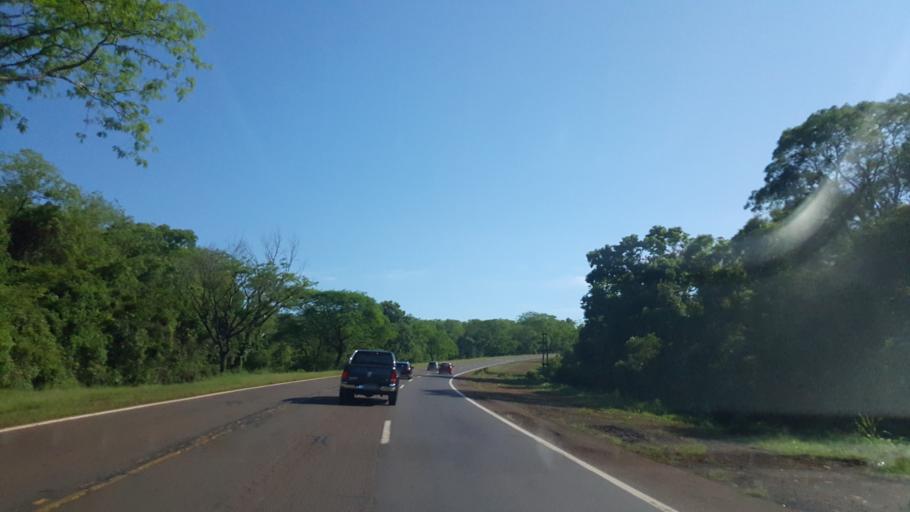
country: AR
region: Misiones
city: Santa Ana
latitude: -27.3602
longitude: -55.5573
